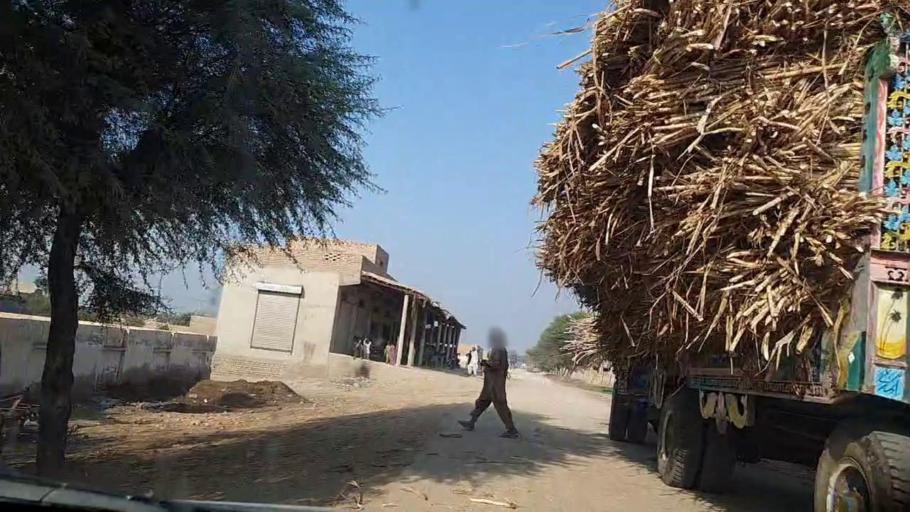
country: PK
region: Sindh
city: Moro
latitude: 26.7861
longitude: 67.9383
